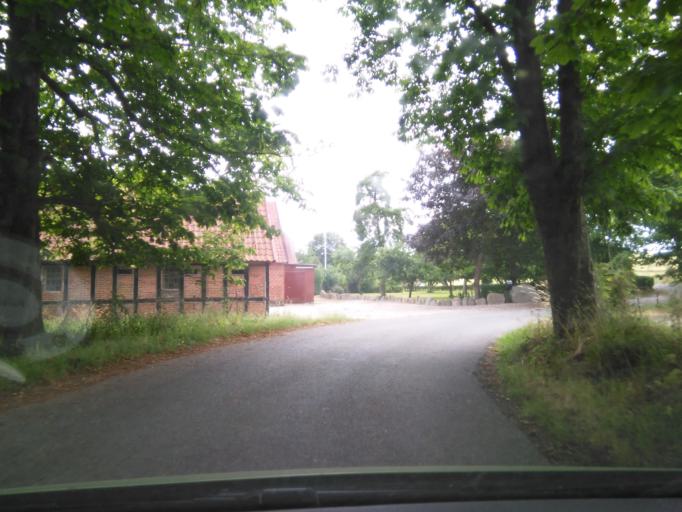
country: DK
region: Central Jutland
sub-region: Arhus Kommune
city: Solbjerg
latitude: 55.9851
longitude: 10.0806
